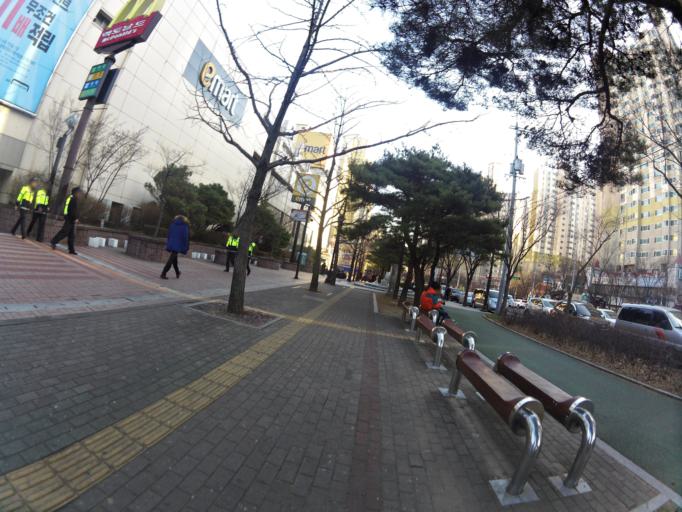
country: KR
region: Daegu
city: Daegu
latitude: 35.8712
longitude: 128.6362
